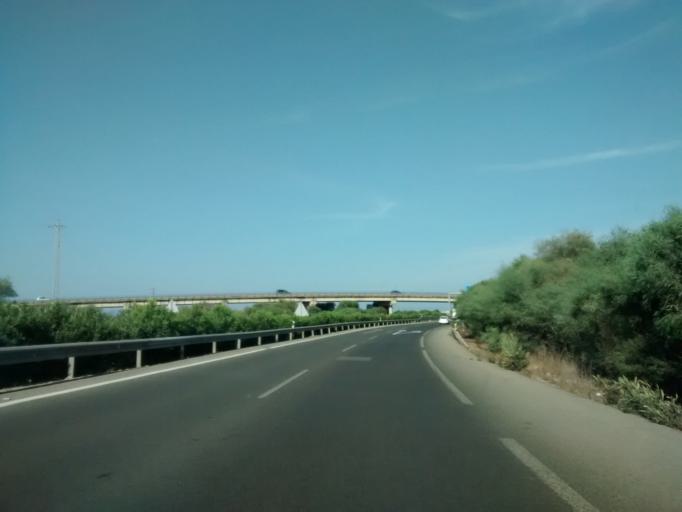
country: ES
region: Andalusia
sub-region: Provincia de Cadiz
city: Chiclana de la Frontera
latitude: 36.4444
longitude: -6.1399
